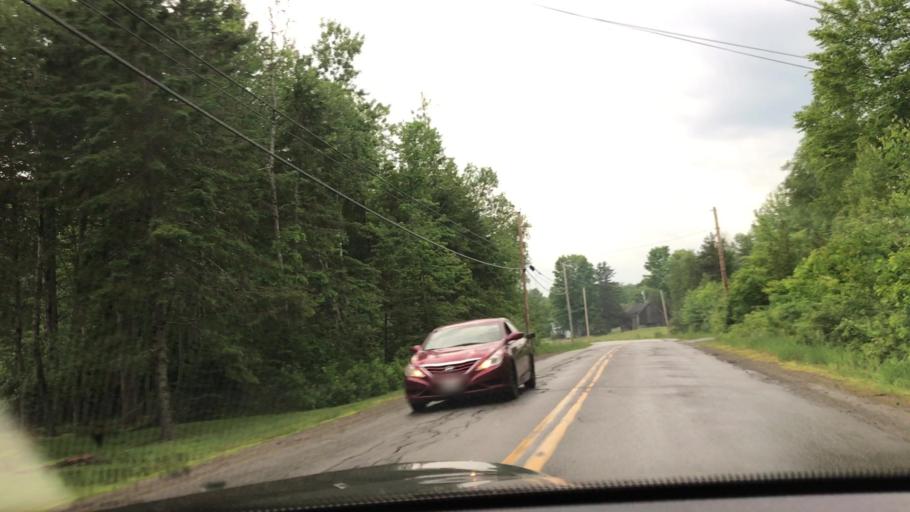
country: US
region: Maine
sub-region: Penobscot County
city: Orono
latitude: 44.8914
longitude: -68.6989
